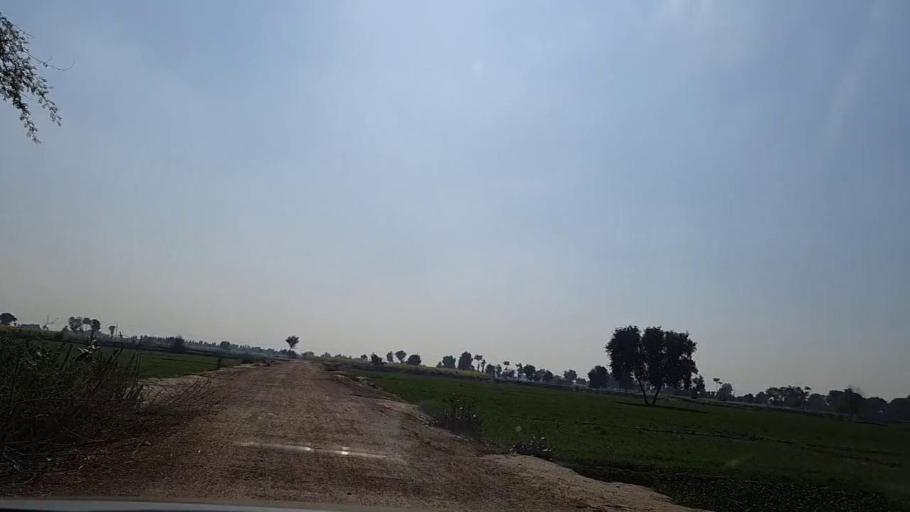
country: PK
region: Sindh
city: Daulatpur
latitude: 26.2862
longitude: 68.0537
